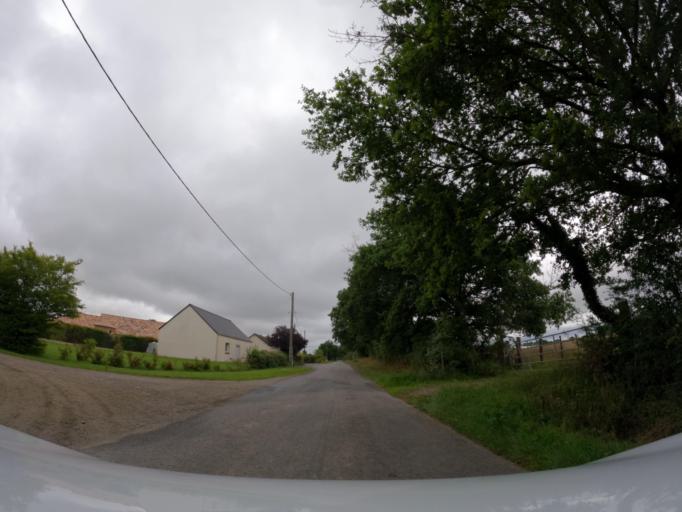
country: FR
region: Pays de la Loire
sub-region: Departement de la Loire-Atlantique
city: Saint-Mars-du-Desert
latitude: 47.3799
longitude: -1.4232
